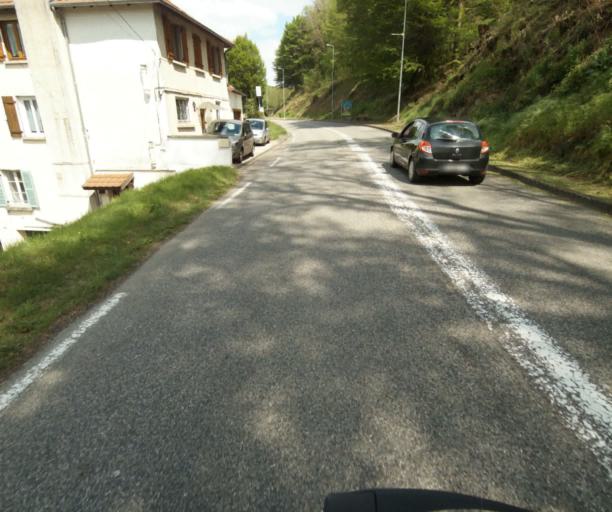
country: FR
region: Limousin
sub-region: Departement de la Correze
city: Tulle
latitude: 45.2810
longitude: 1.7690
